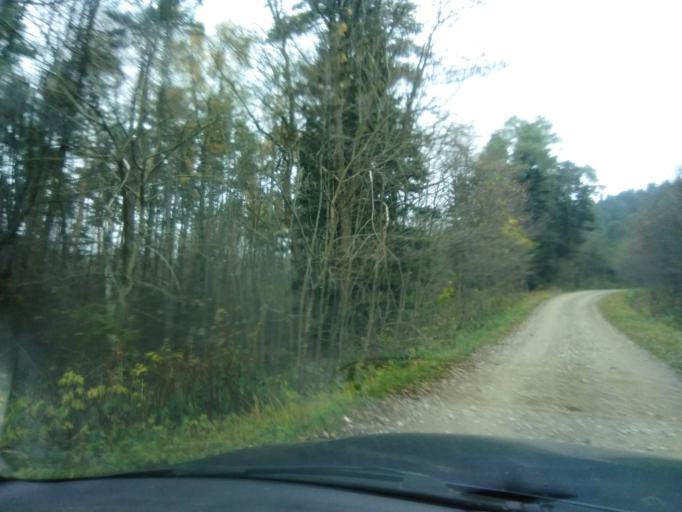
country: PL
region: Subcarpathian Voivodeship
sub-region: Powiat strzyzowski
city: Wysoka Strzyzowska
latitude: 49.7898
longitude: 21.7678
